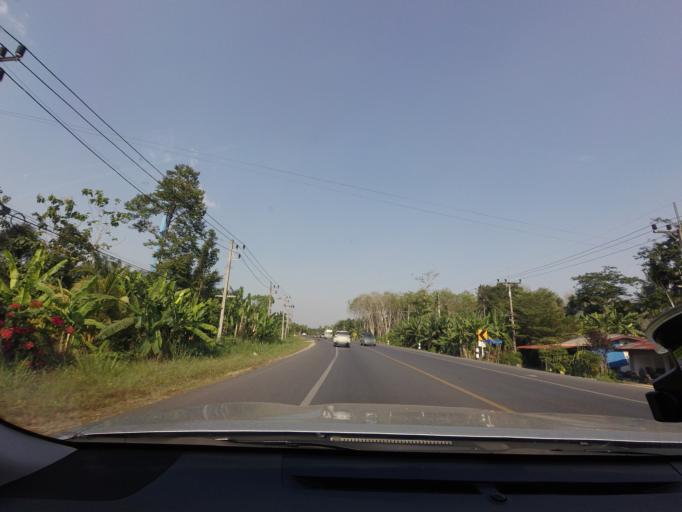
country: TH
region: Surat Thani
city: Phrasaeng
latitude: 8.5697
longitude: 99.1983
